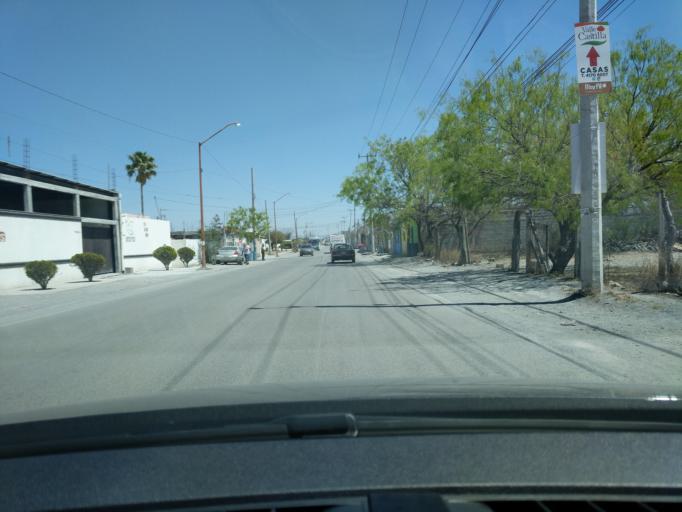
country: MX
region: Nuevo Leon
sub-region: Salinas Victoria
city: Emiliano Zapata
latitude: 25.9091
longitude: -100.2744
